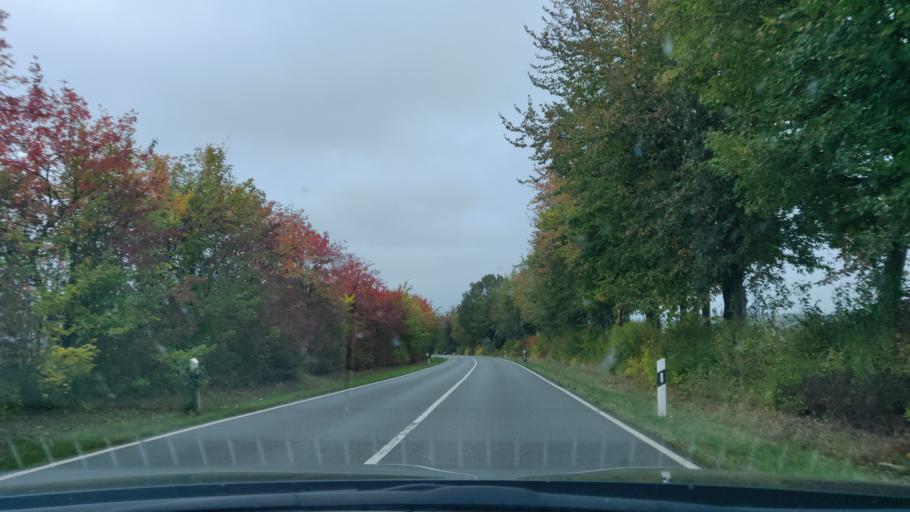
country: DE
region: Hesse
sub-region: Regierungsbezirk Kassel
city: Baunatal
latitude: 51.2376
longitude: 9.4208
